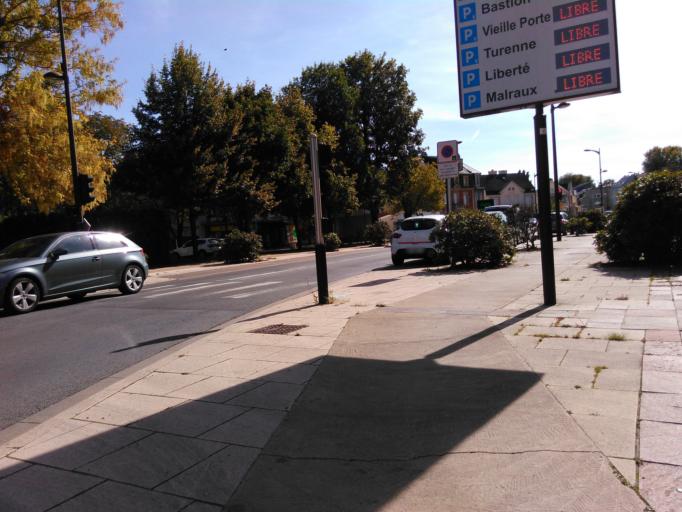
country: FR
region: Lorraine
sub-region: Departement de la Moselle
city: Thionville
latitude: 49.3674
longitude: 6.1691
